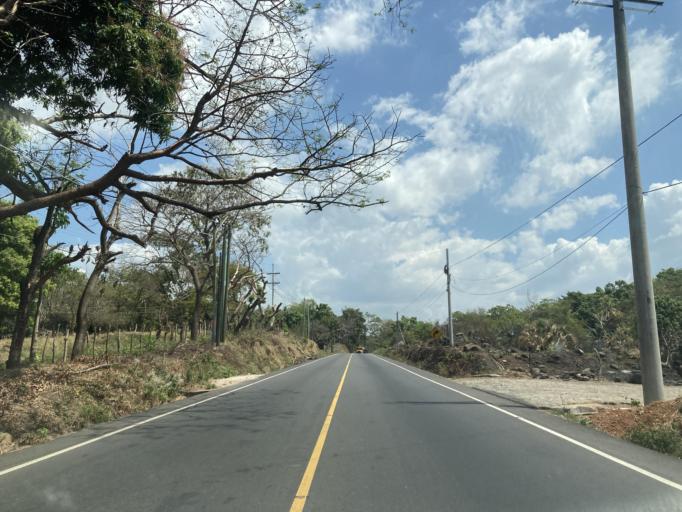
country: GT
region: Santa Rosa
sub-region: Municipio de Taxisco
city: Taxisco
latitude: 14.0657
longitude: -90.4457
